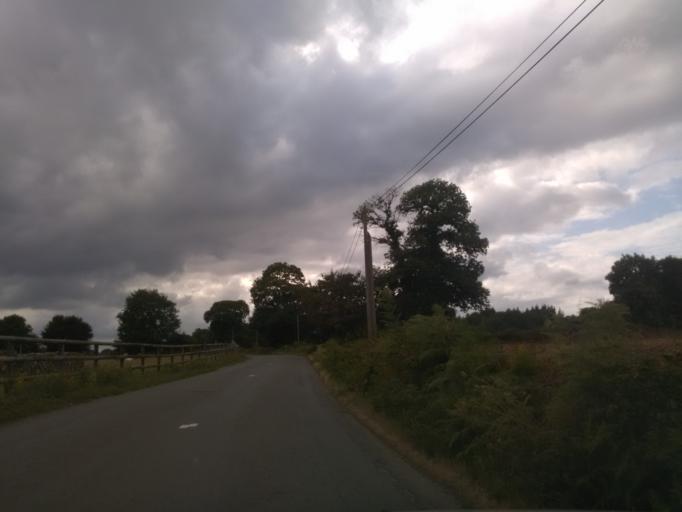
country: FR
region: Brittany
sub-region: Departement d'Ille-et-Vilaine
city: Dinge
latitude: 48.3553
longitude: -1.7378
